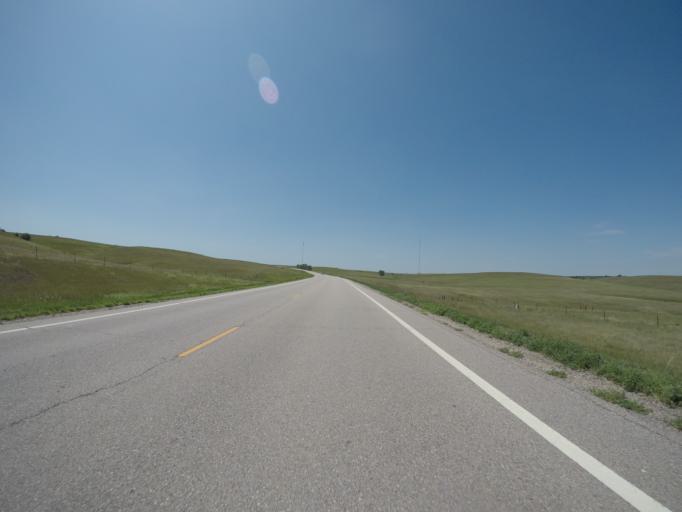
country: US
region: Kansas
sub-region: Osborne County
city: Osborne
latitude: 39.4903
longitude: -98.6965
